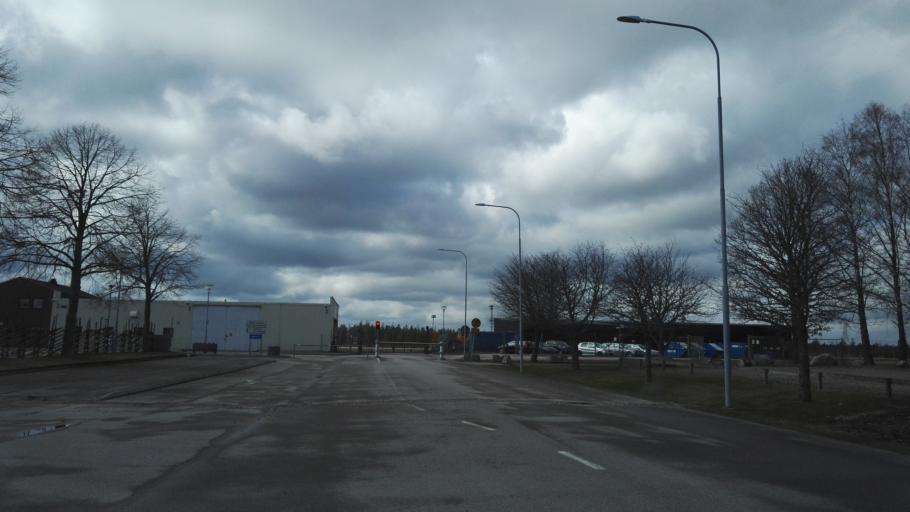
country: SE
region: Kronoberg
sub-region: Vaxjo Kommun
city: Vaexjoe
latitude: 56.9257
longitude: 14.7334
